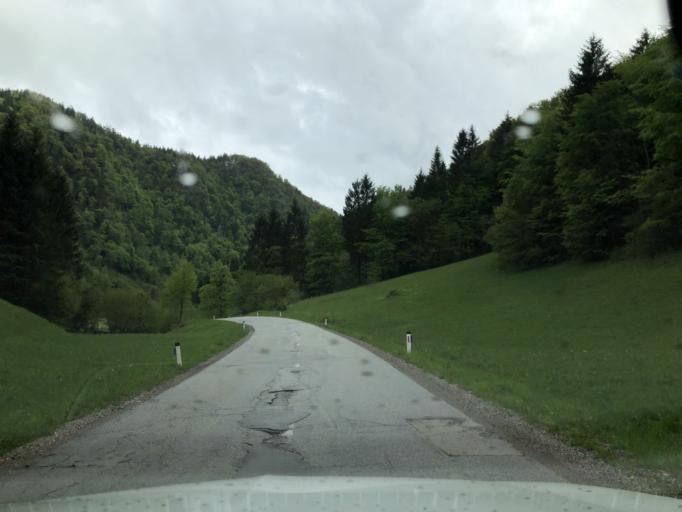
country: SI
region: Jesenice
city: Slovenski Javornik
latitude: 46.4085
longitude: 14.0774
